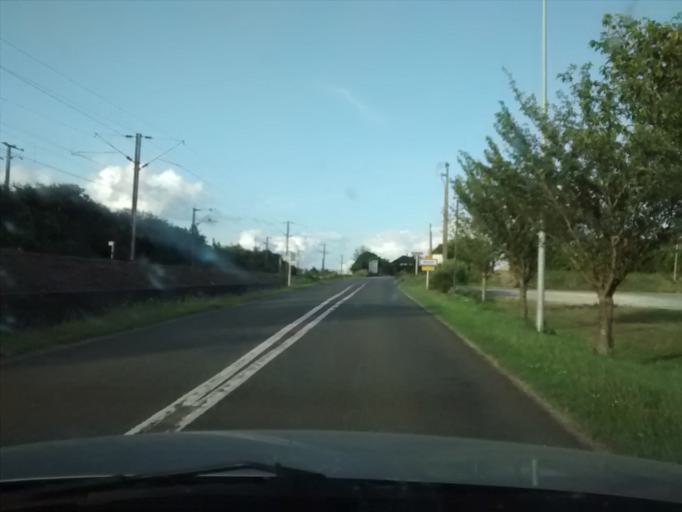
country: FR
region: Pays de la Loire
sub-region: Departement de la Mayenne
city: Montsurs
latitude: 48.1551
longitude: -0.4837
